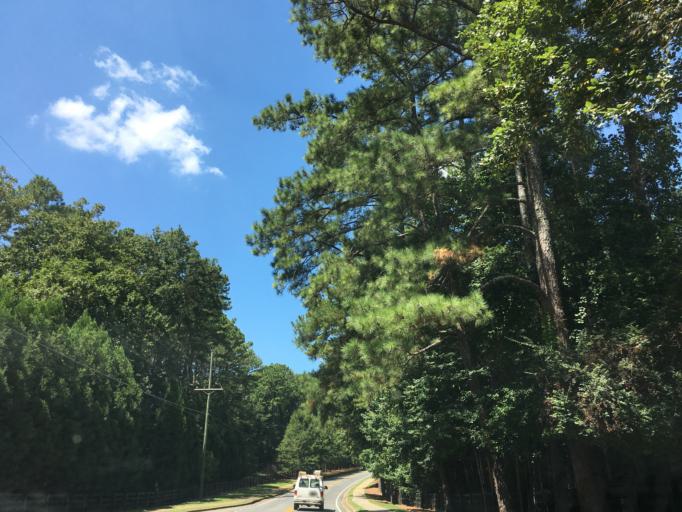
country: US
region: Georgia
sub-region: Fulton County
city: Milton
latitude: 34.1188
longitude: -84.3267
